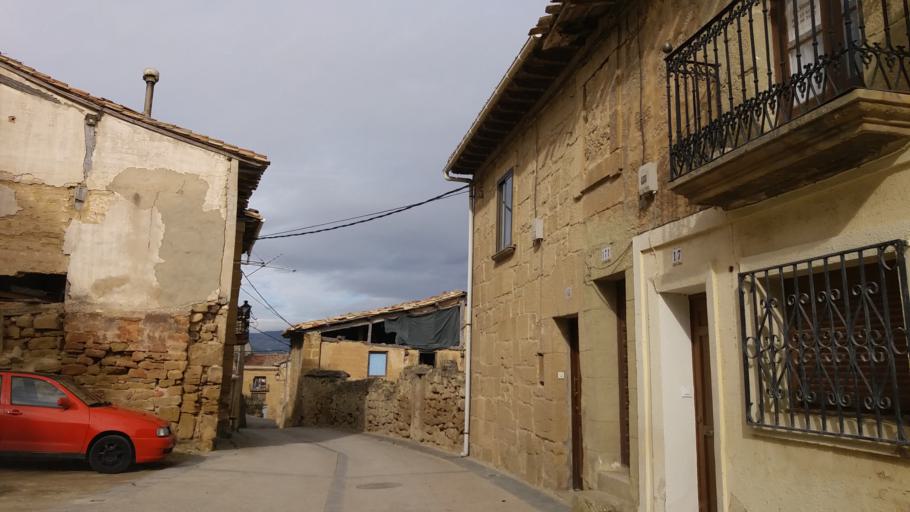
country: ES
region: La Rioja
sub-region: Provincia de La Rioja
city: San Vicente de la Sonsierra
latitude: 42.5601
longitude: -2.7565
